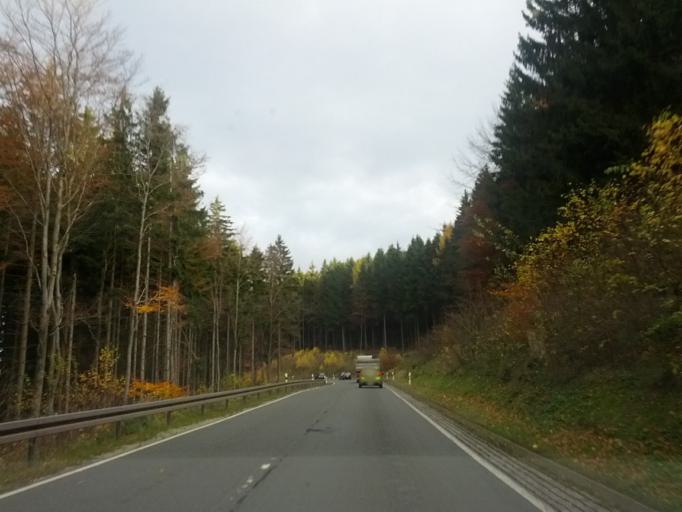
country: DE
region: Thuringia
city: Tabarz
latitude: 50.8648
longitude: 10.4847
